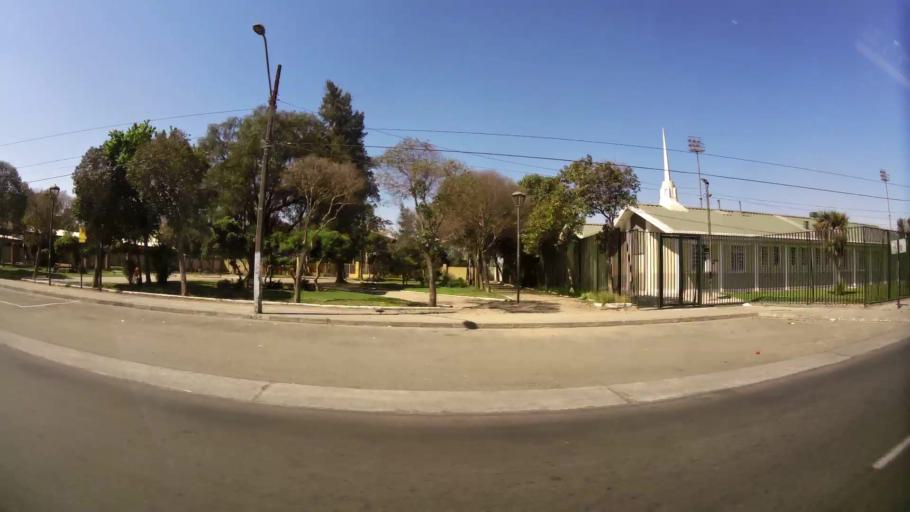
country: CL
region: Santiago Metropolitan
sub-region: Provincia de Santiago
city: Lo Prado
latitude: -33.5071
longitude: -70.7349
